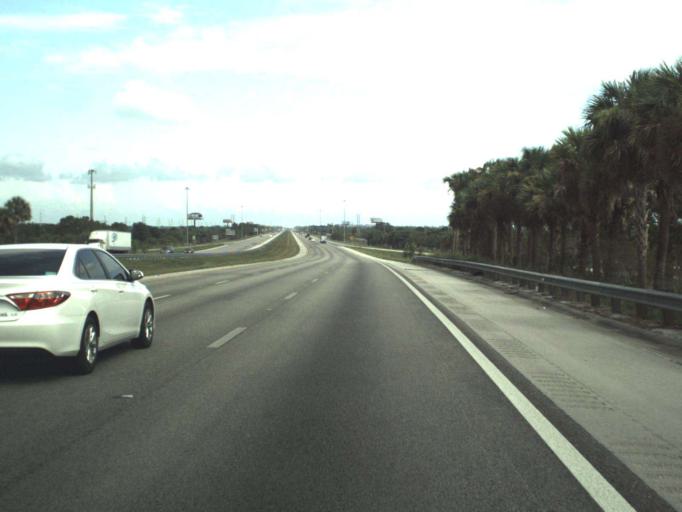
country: US
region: Florida
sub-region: Saint Lucie County
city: Lakewood Park
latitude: 27.5229
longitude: -80.4516
